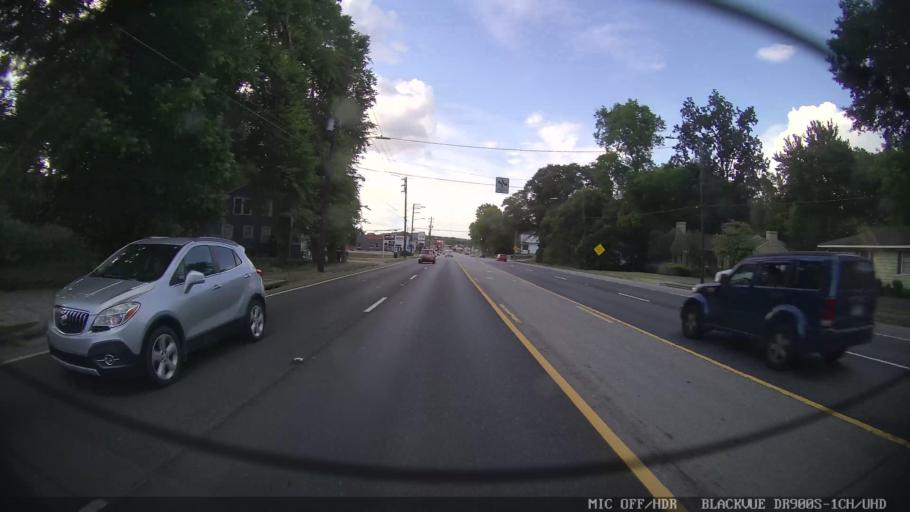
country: US
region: Georgia
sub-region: Floyd County
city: Rome
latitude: 34.2404
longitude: -85.1614
